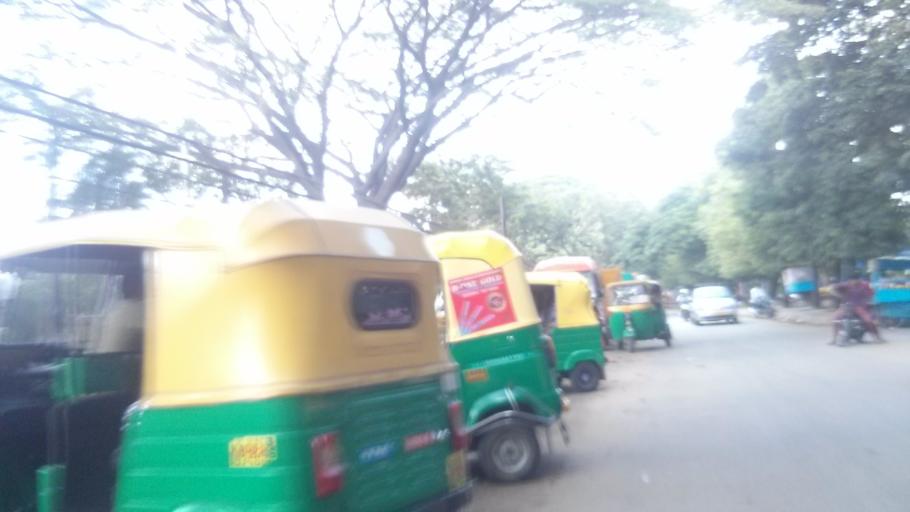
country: IN
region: Karnataka
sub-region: Bangalore Urban
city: Bangalore
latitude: 12.9825
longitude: 77.6362
